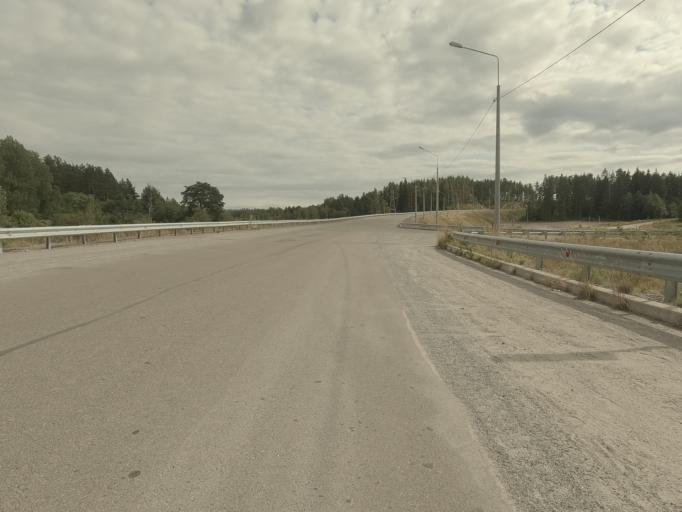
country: RU
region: Leningrad
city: Kamennogorsk
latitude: 60.9648
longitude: 29.1410
